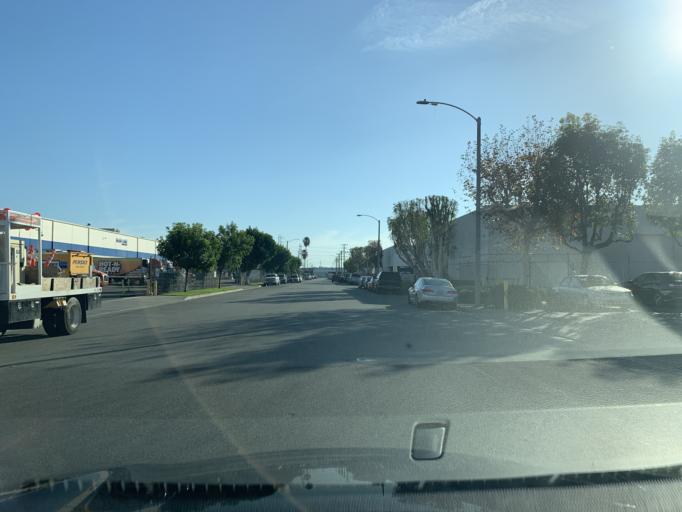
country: US
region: California
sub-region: Orange County
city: Anaheim
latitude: 33.8141
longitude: -117.9002
